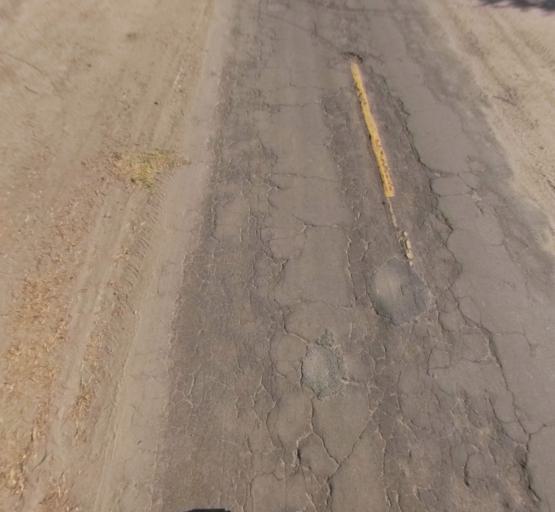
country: US
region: California
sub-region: Madera County
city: Madera
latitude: 36.9396
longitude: -120.1194
